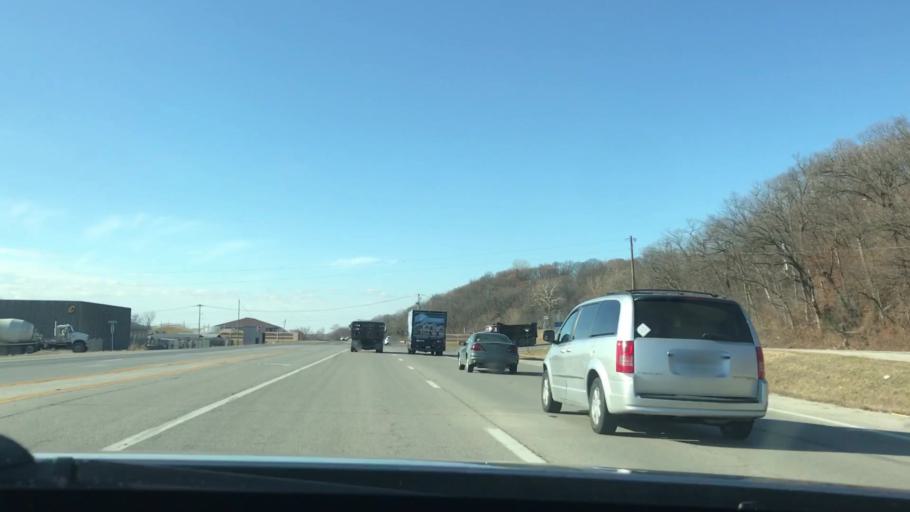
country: US
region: Missouri
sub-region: Platte County
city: Riverside
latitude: 39.1771
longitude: -94.6457
